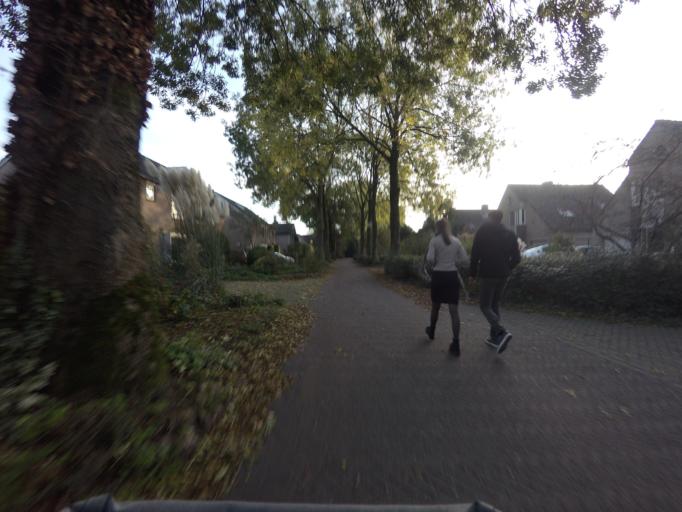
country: NL
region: Utrecht
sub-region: Gemeente De Bilt
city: De Bilt
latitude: 52.1528
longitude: 5.1807
